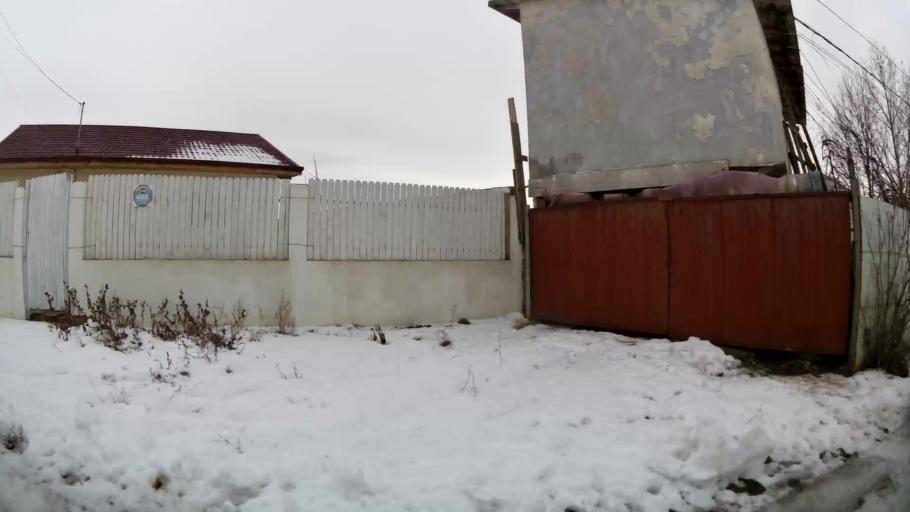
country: RO
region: Ilfov
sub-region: Comuna Pantelimon
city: Pantelimon
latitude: 44.4657
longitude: 26.2044
